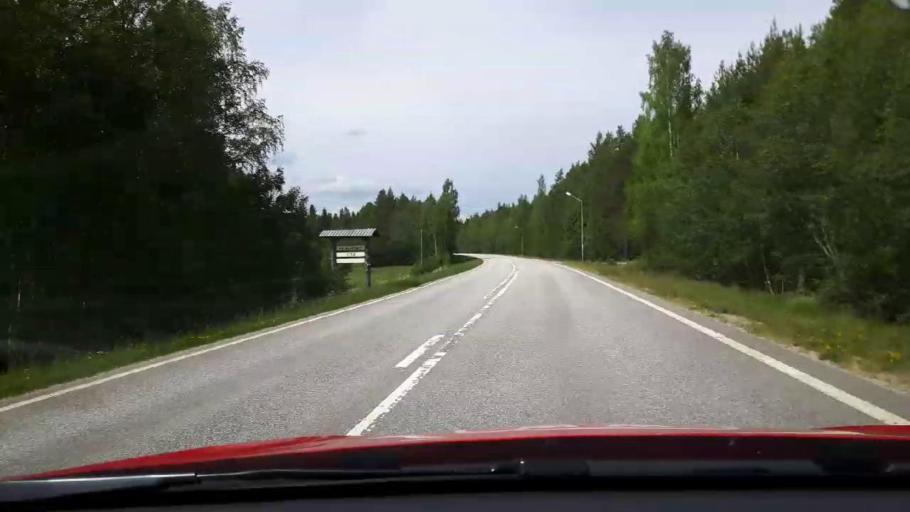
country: SE
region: Jaemtland
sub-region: Harjedalens Kommun
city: Sveg
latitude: 62.1342
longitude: 14.0511
